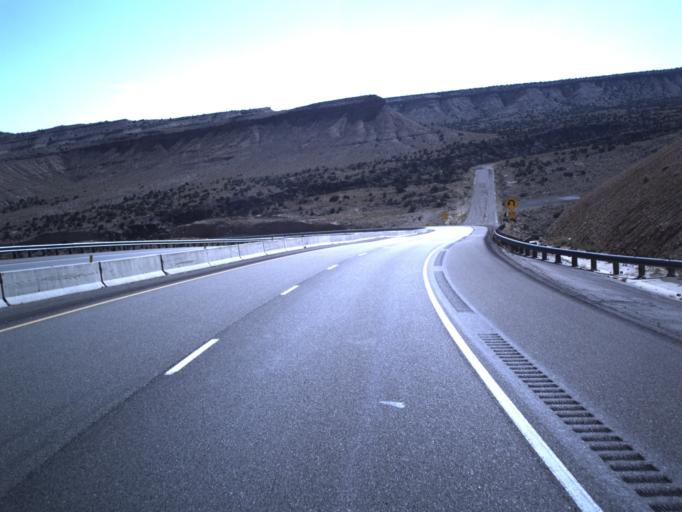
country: US
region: Utah
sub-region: Carbon County
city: East Carbon City
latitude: 38.9342
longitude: -110.4638
